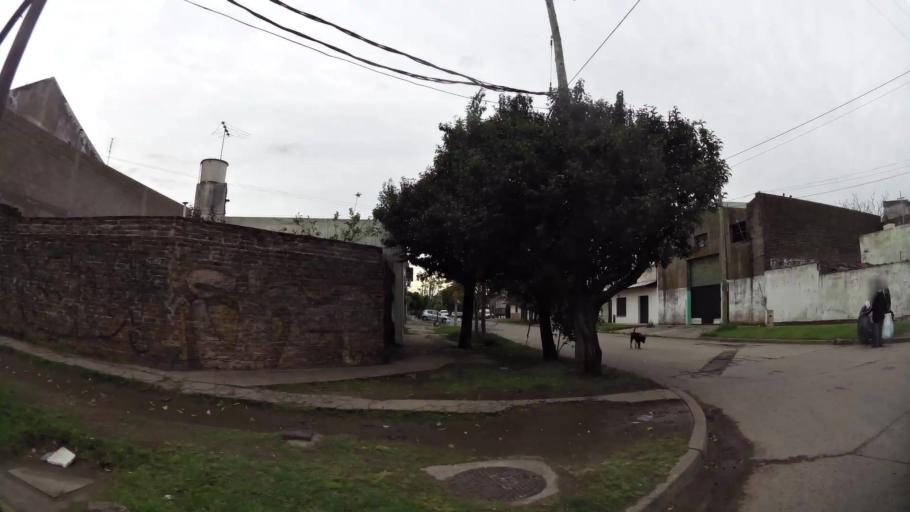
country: AR
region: Buenos Aires
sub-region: Partido de Lanus
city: Lanus
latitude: -34.7239
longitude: -58.3541
